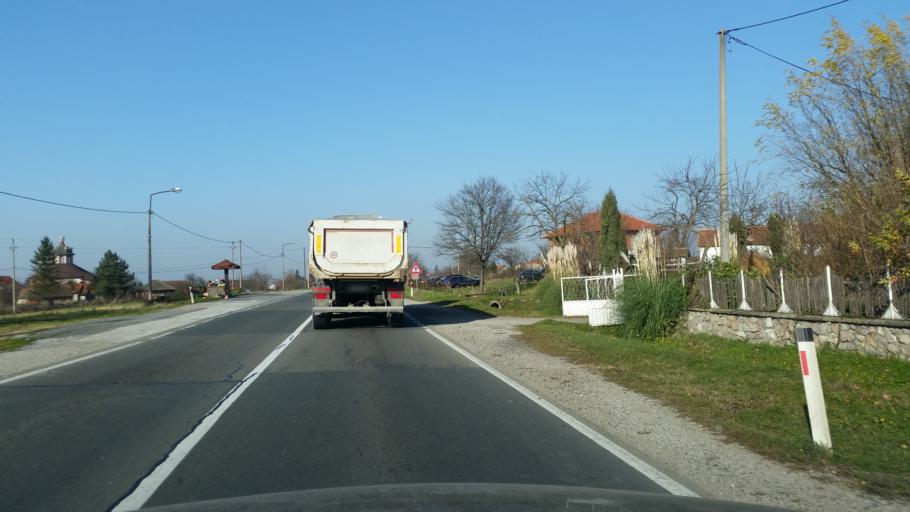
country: RS
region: Central Serbia
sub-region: Kolubarski Okrug
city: Lajkovac
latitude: 44.3503
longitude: 20.1924
